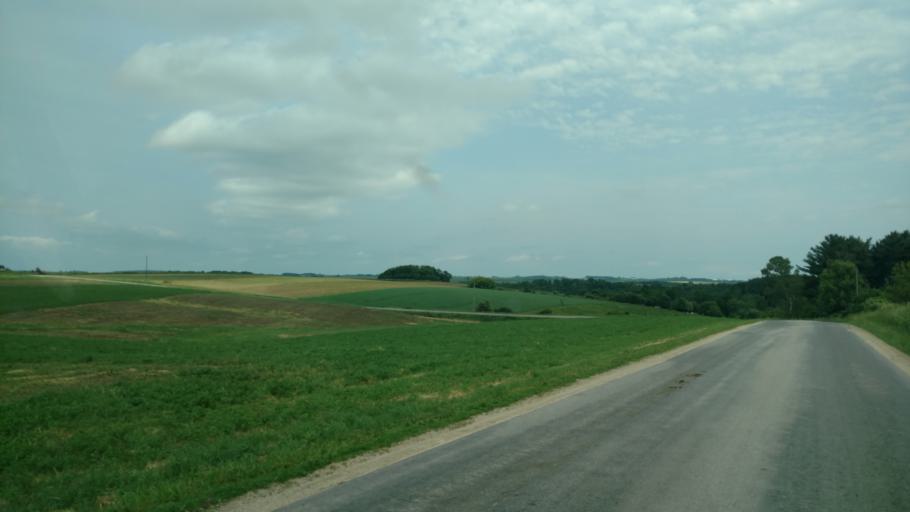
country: US
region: Wisconsin
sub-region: Monroe County
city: Cashton
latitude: 43.7131
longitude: -90.7104
